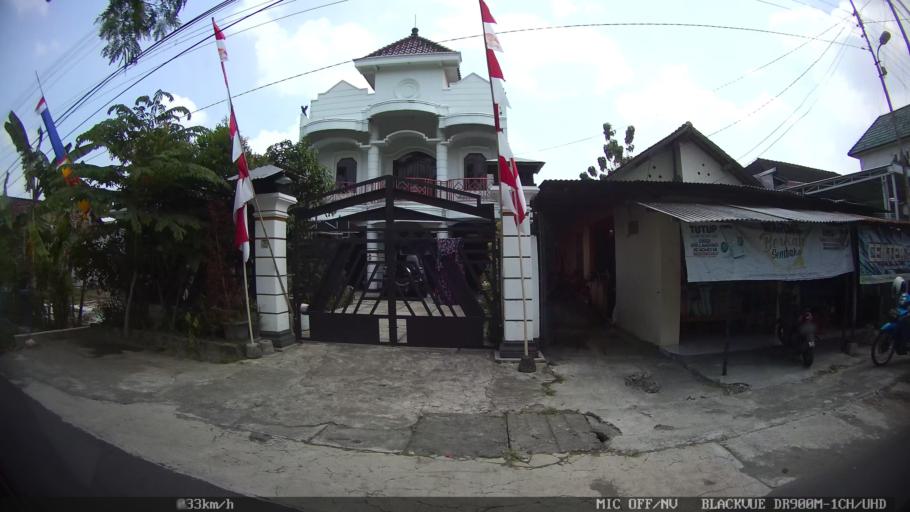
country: ID
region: Daerah Istimewa Yogyakarta
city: Yogyakarta
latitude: -7.8120
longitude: 110.3989
